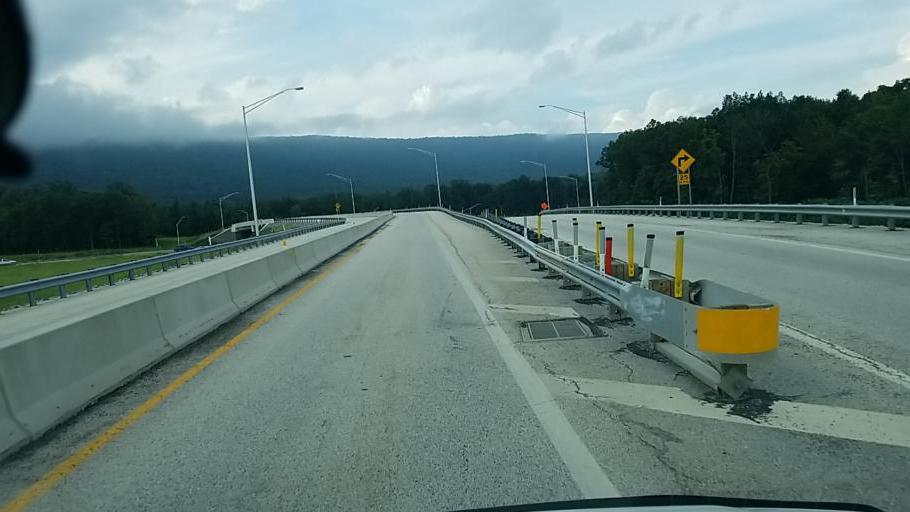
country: US
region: Pennsylvania
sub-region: Franklin County
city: Doylestown
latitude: 40.1564
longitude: -77.6137
